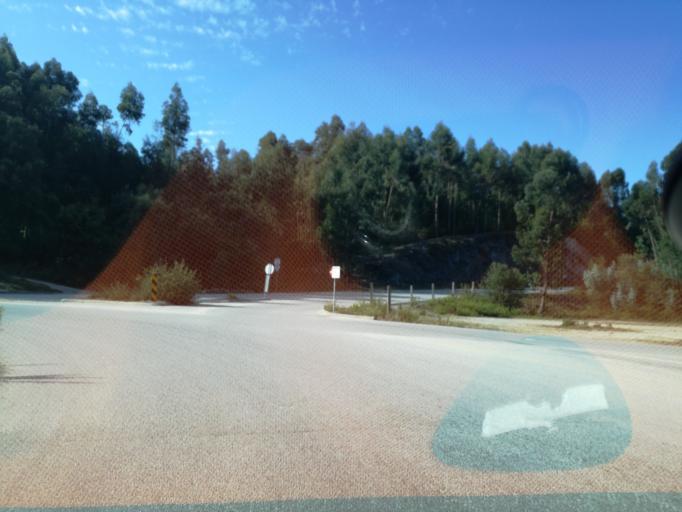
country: PT
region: Porto
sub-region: Pacos de Ferreira
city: Seroa
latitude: 41.2837
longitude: -8.4244
